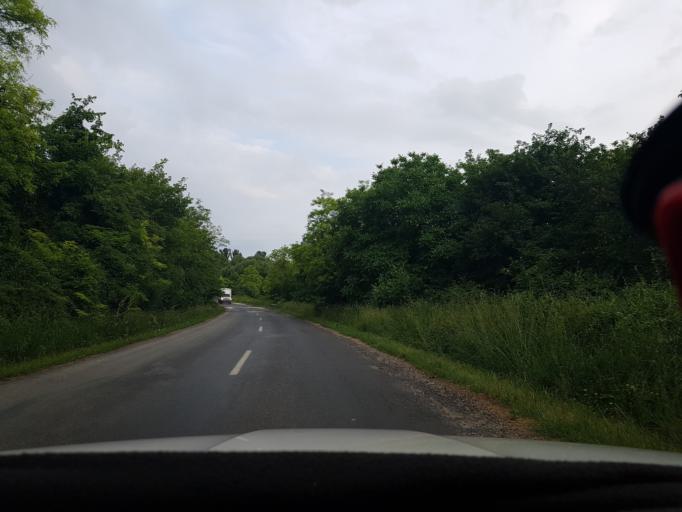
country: HU
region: Pest
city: Perbal
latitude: 47.6405
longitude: 18.7470
